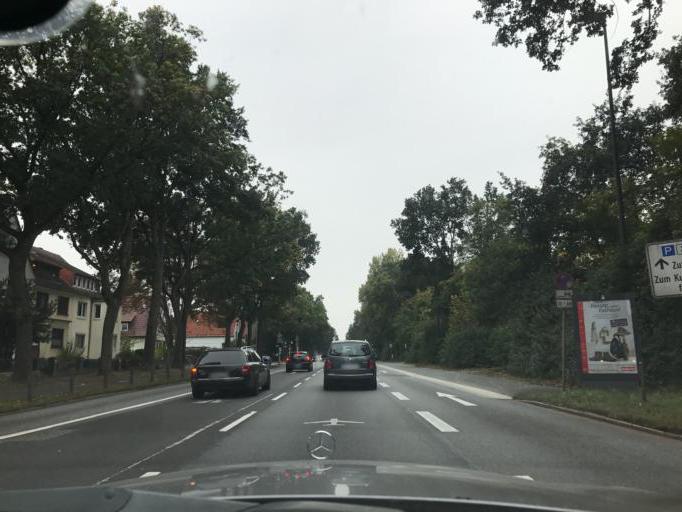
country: DE
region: Bremen
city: Bremen
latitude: 53.0586
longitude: 8.7941
